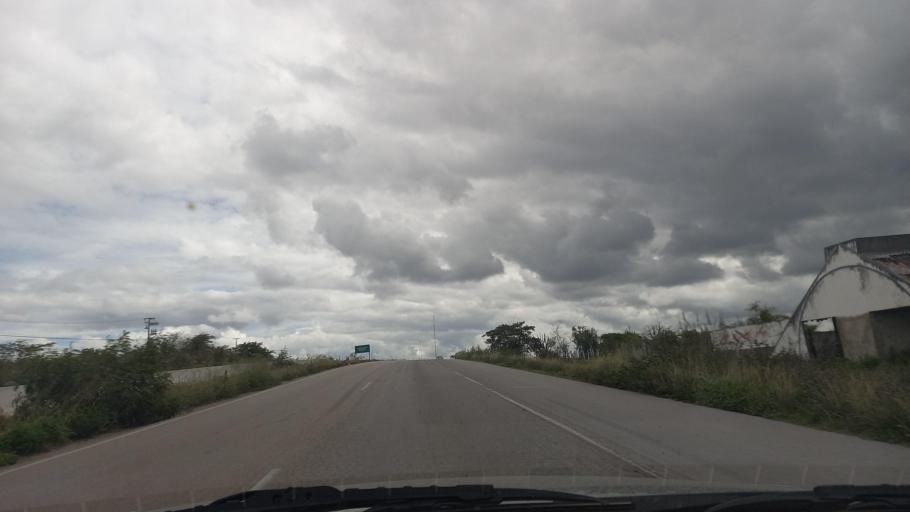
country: BR
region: Pernambuco
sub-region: Caruaru
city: Caruaru
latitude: -8.3281
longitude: -36.1191
